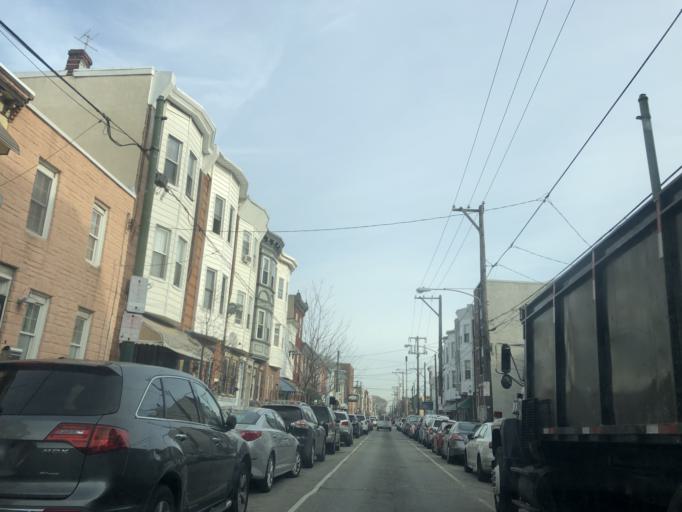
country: US
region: Pennsylvania
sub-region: Philadelphia County
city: Philadelphia
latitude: 39.9279
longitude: -75.1585
